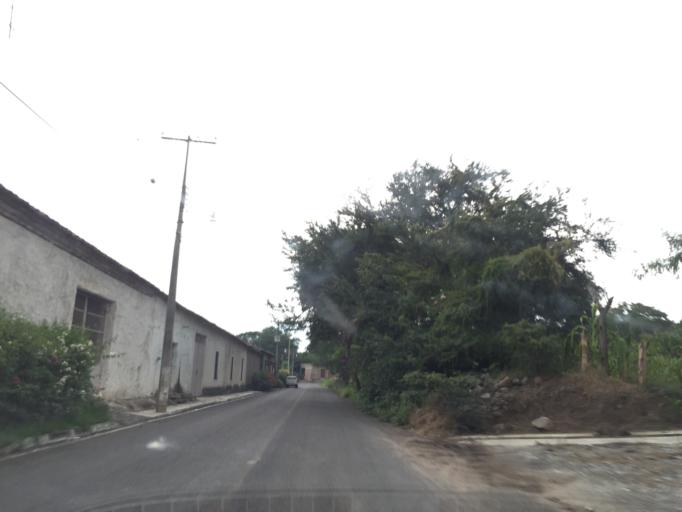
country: MX
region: Colima
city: Comala
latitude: 19.3373
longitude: -103.7754
